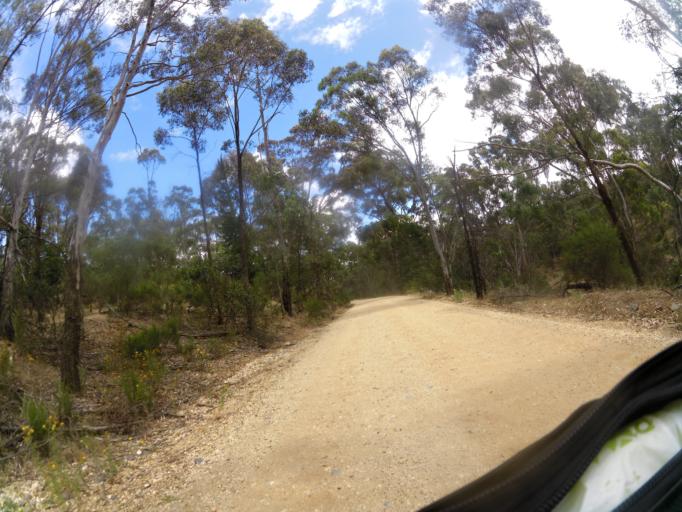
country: AU
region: Victoria
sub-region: Mount Alexander
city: Castlemaine
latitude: -37.0315
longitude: 144.2565
